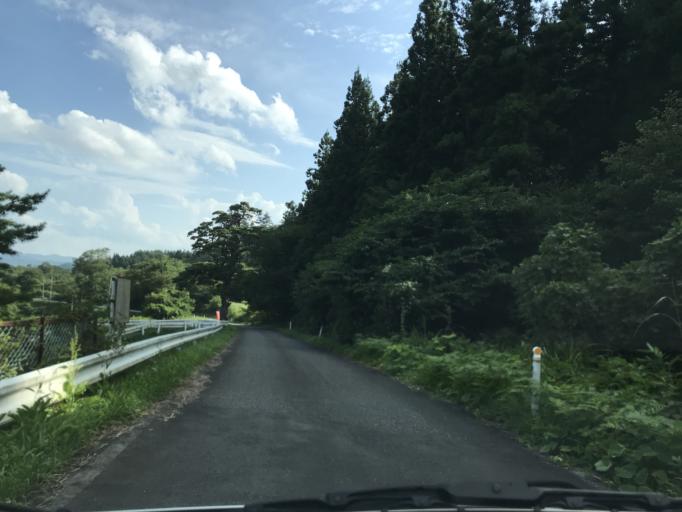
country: JP
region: Iwate
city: Ofunato
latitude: 38.9718
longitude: 141.4698
